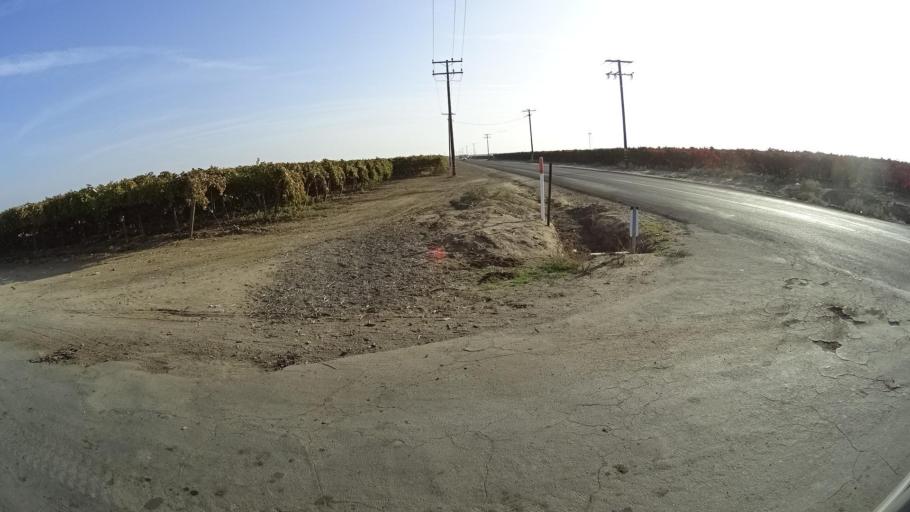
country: US
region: California
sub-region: Kern County
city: McFarland
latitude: 35.6892
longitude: -119.1870
